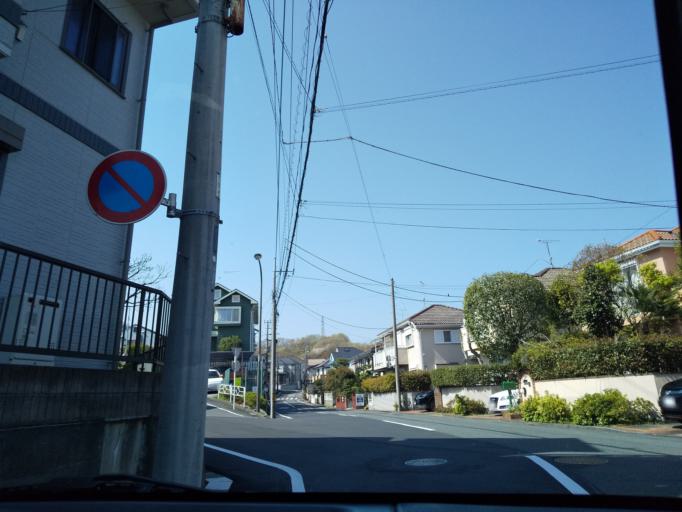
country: JP
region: Tokyo
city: Hino
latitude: 35.6419
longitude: 139.3749
